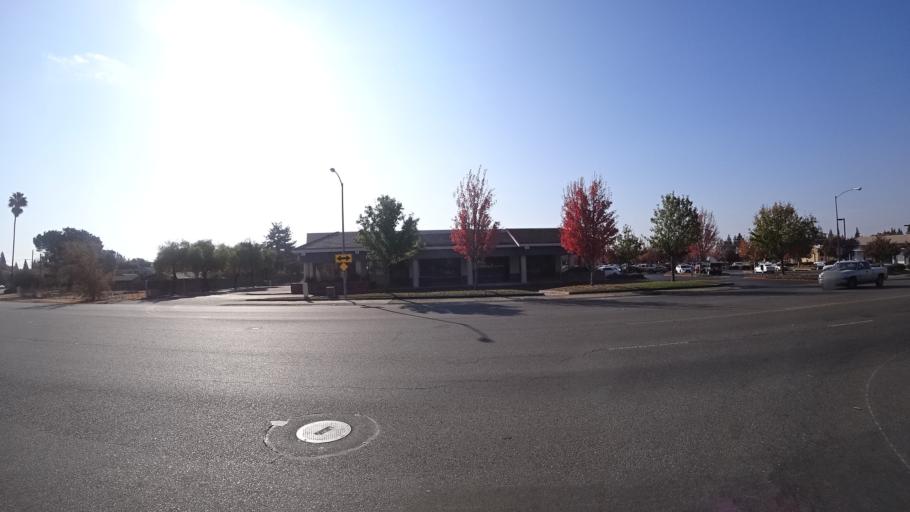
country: US
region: California
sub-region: Sacramento County
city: Citrus Heights
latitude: 38.7078
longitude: -121.2695
